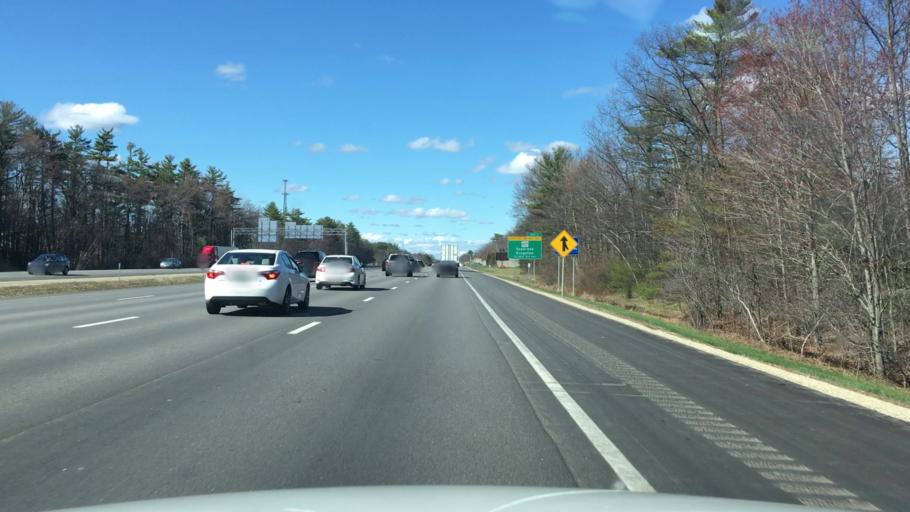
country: US
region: New Hampshire
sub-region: Rockingham County
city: Seabrook
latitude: 42.8846
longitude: -70.8819
